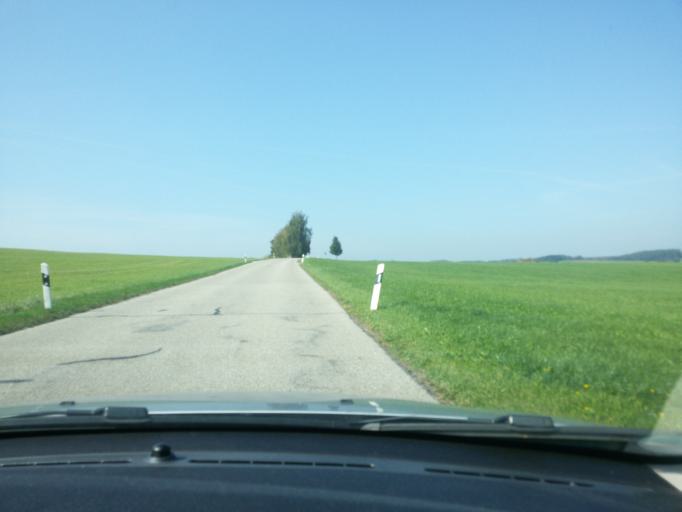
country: DE
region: Bavaria
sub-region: Swabia
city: Scherstetten
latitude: 48.1831
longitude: 10.6532
